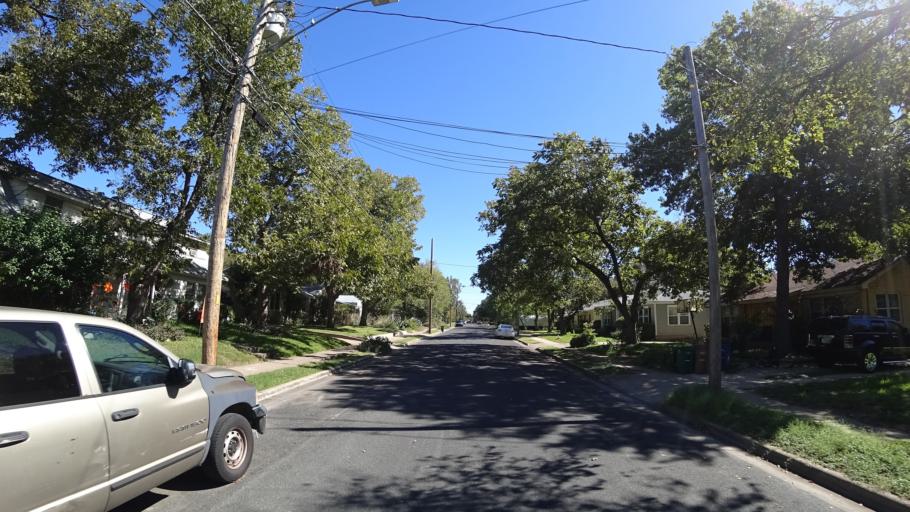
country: US
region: Texas
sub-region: Travis County
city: Austin
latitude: 30.3371
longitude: -97.7302
